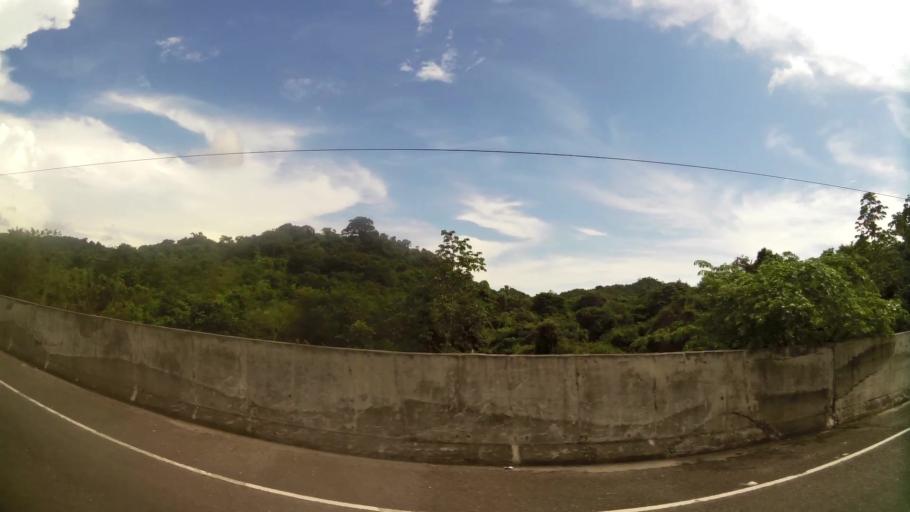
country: PA
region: Panama
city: San Miguelito
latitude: 9.0780
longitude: -79.4787
